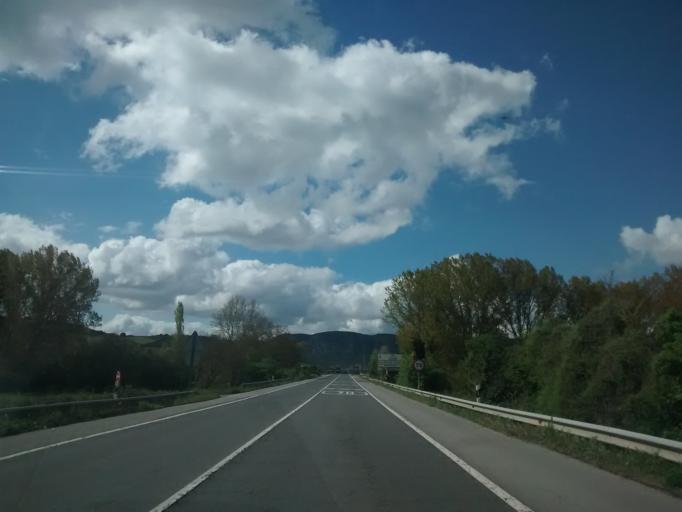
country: ES
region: Basque Country
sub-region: Provincia de Alava
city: Zambrana
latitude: 42.6820
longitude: -2.8841
